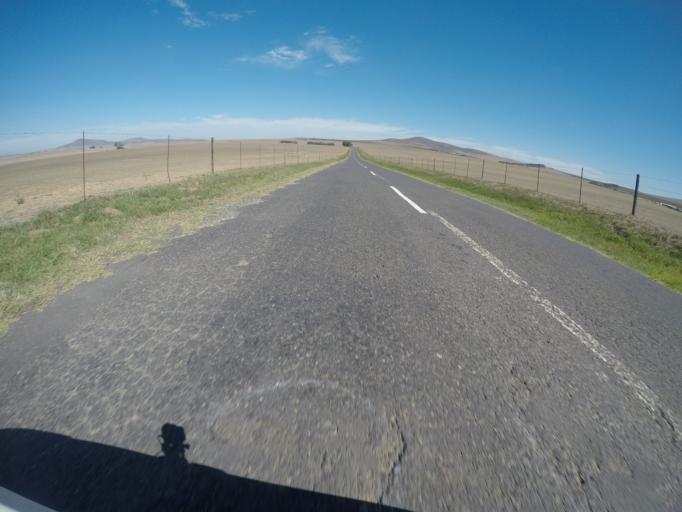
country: ZA
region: Western Cape
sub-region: City of Cape Town
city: Atlantis
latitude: -33.6868
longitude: 18.5981
